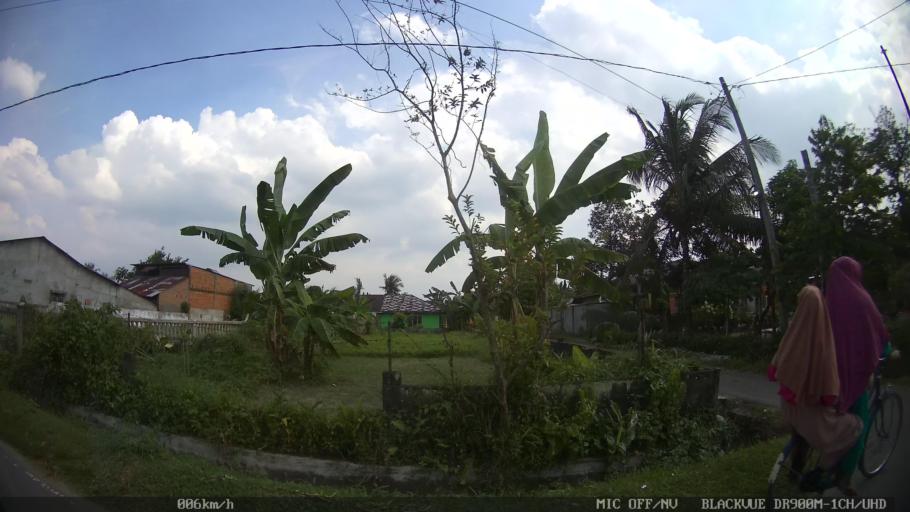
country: ID
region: North Sumatra
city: Binjai
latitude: 3.6132
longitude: 98.5279
